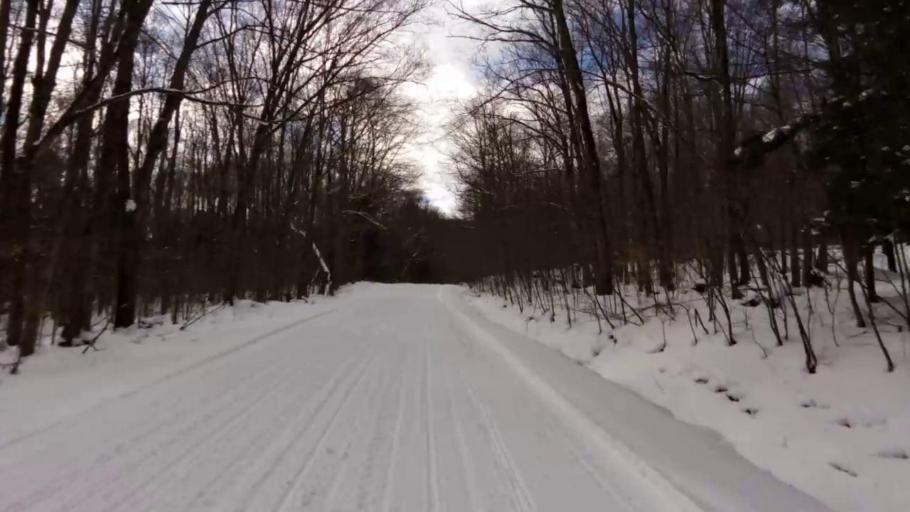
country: US
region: Pennsylvania
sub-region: McKean County
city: Bradford
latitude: 42.0254
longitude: -78.6882
